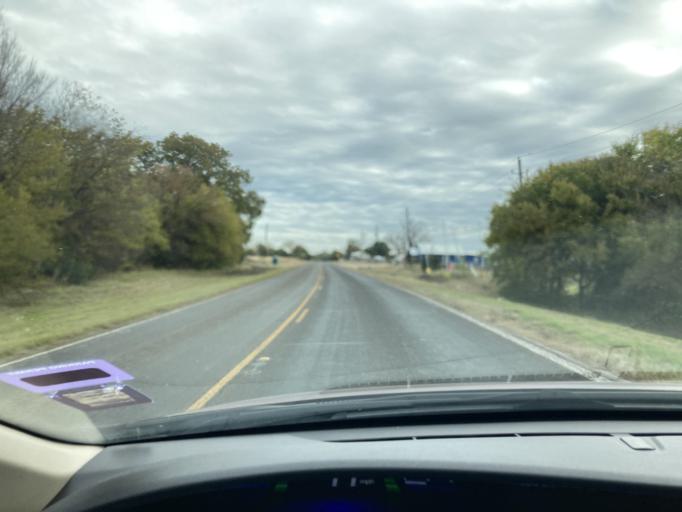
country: US
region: Texas
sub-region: Navarro County
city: Corsicana
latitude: 32.0656
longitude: -96.5018
